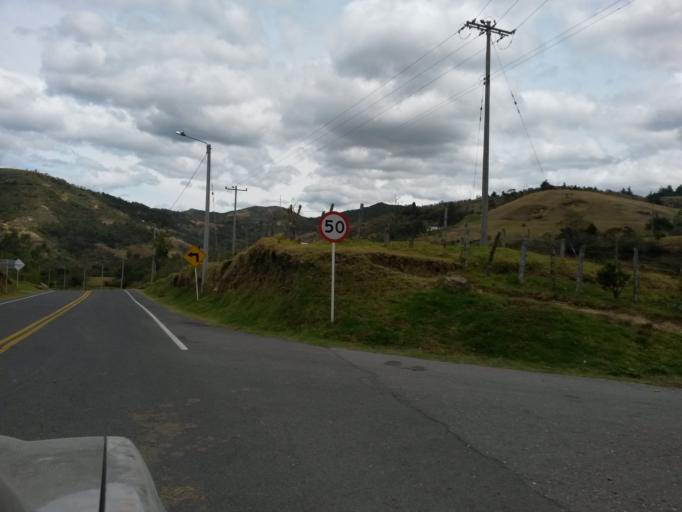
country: CO
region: Cauca
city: Totoro
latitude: 2.5109
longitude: -76.4069
